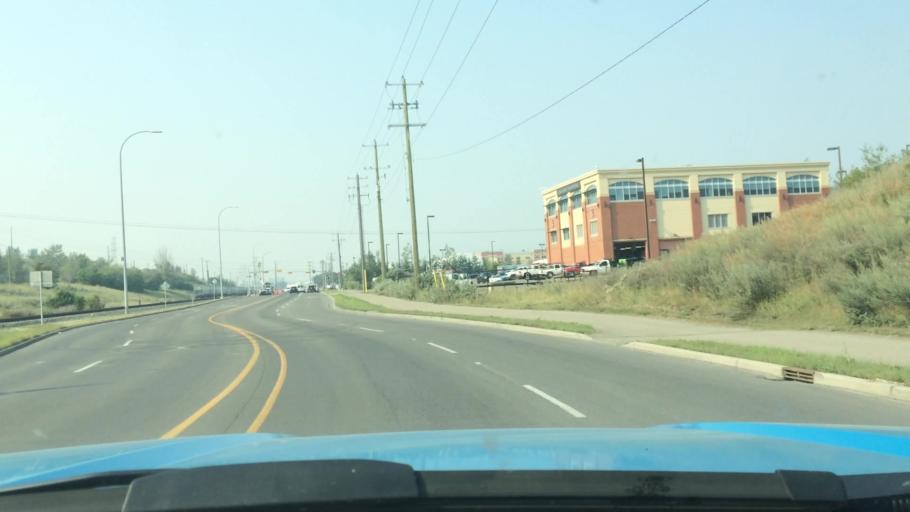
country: CA
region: Alberta
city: Calgary
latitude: 51.0301
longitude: -114.0418
